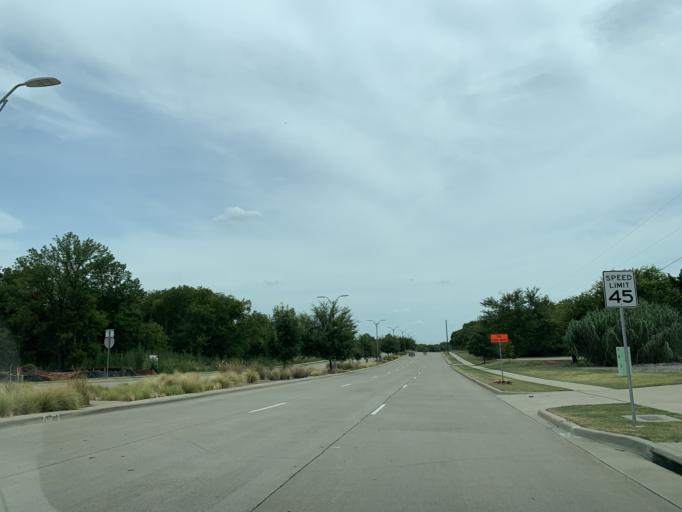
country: US
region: Texas
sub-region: Dallas County
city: Grand Prairie
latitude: 32.6734
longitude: -97.0237
